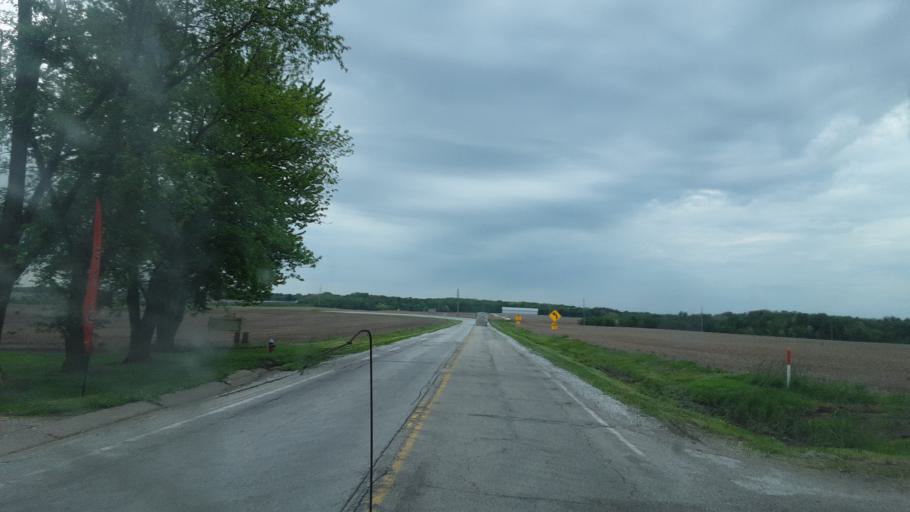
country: US
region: Illinois
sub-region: Fulton County
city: Astoria
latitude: 40.3608
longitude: -90.4253
